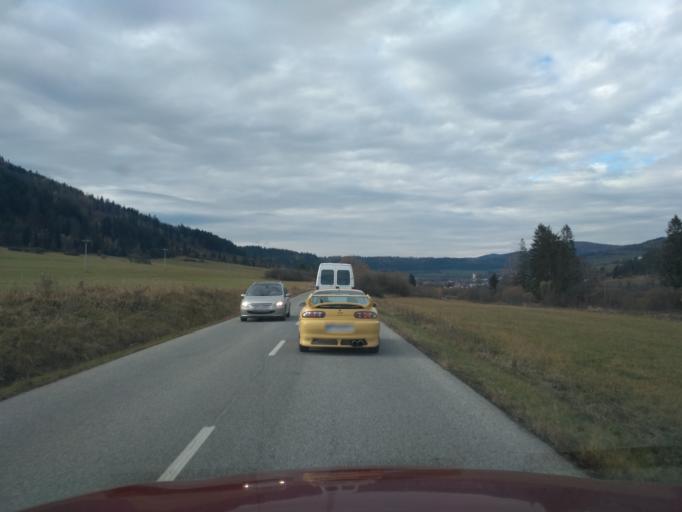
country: SK
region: Kosicky
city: Krompachy
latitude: 48.7997
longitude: 20.7391
